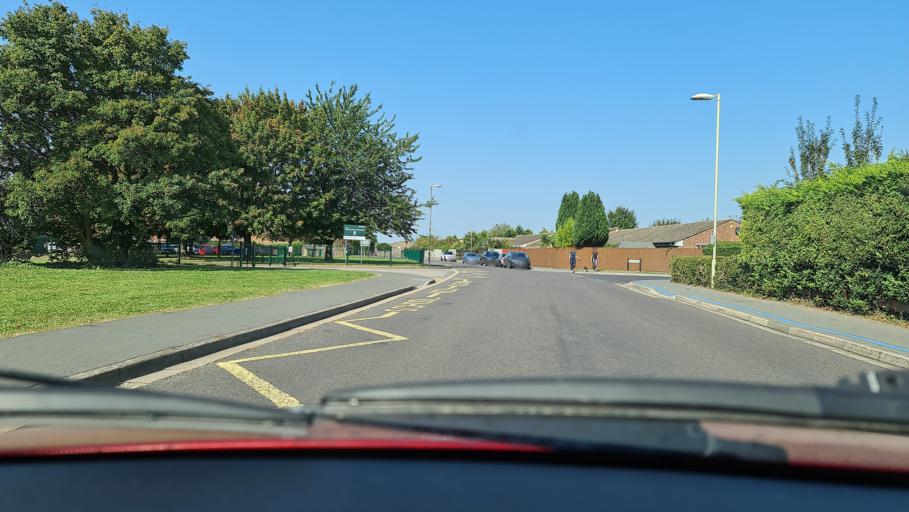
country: GB
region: England
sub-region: Oxfordshire
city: Bicester
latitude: 51.9061
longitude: -1.1714
